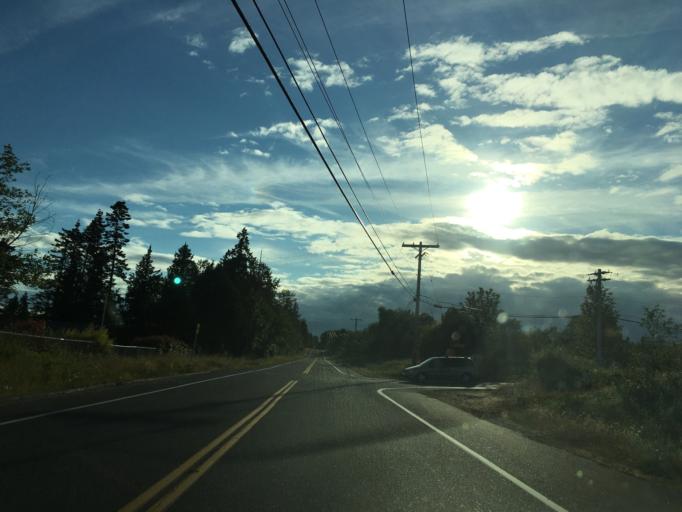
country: US
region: Washington
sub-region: Whatcom County
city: Birch Bay
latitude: 48.9437
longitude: -122.7808
